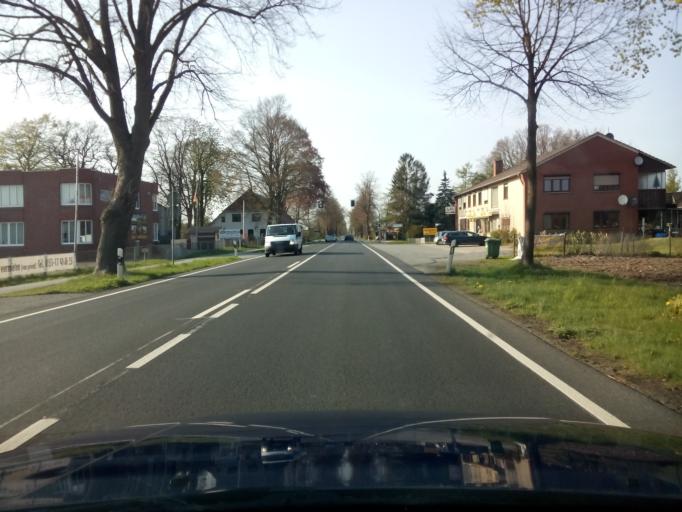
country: DE
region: Lower Saxony
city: Syke
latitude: 52.9701
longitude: 8.7948
